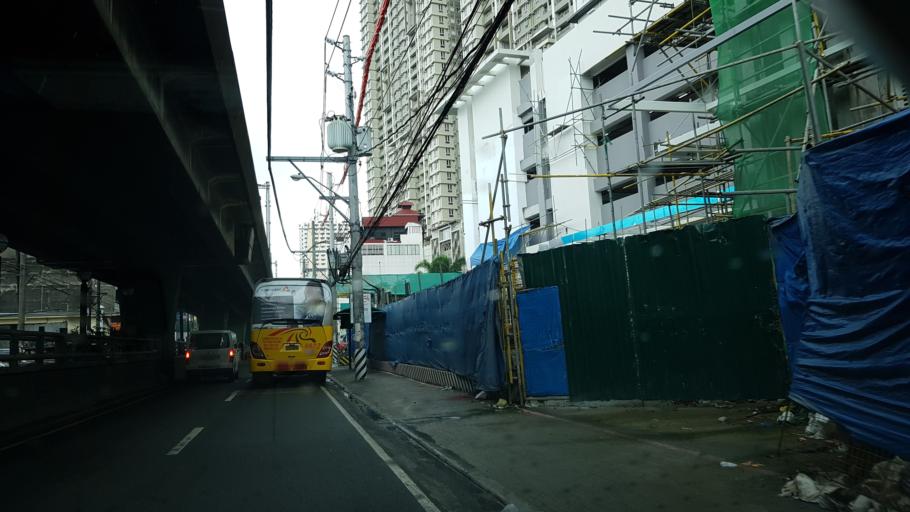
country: PH
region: Metro Manila
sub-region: Makati City
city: Makati City
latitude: 14.5584
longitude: 120.9966
